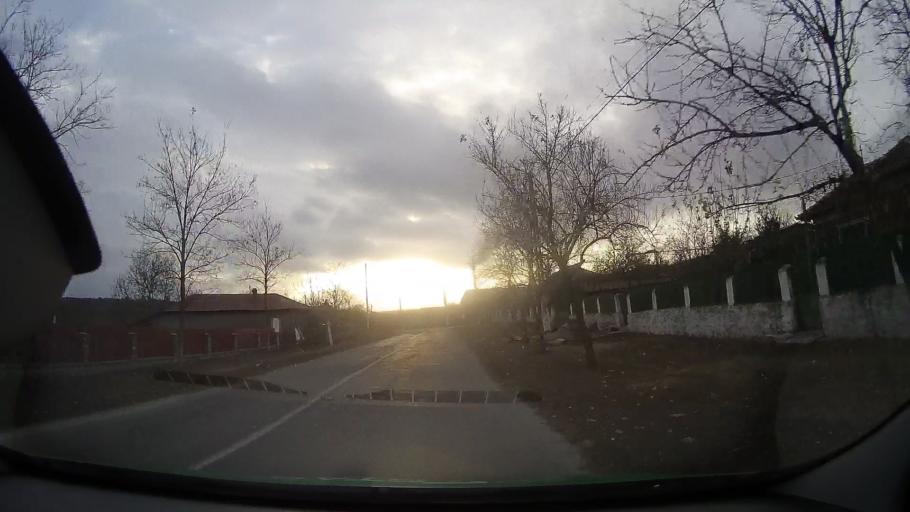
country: RO
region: Constanta
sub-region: Comuna Adamclisi
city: Adamclisi
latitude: 44.0436
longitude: 27.9570
